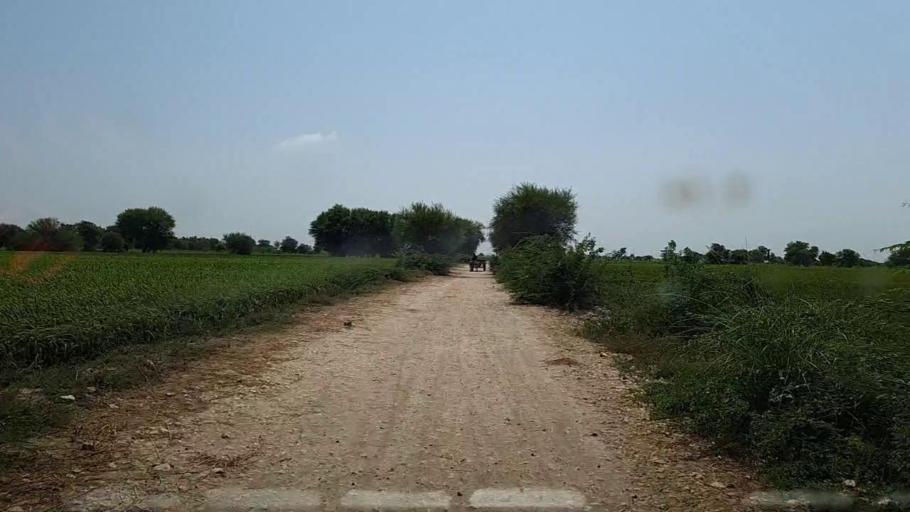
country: PK
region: Sindh
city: Kario
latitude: 24.6443
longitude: 68.4861
